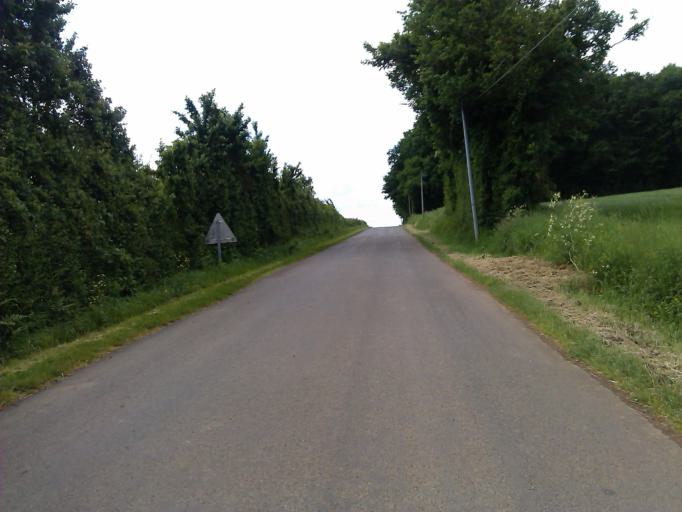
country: FR
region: Poitou-Charentes
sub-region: Departement de la Charente
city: Champagne-Mouton
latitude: 46.0515
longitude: 0.4688
